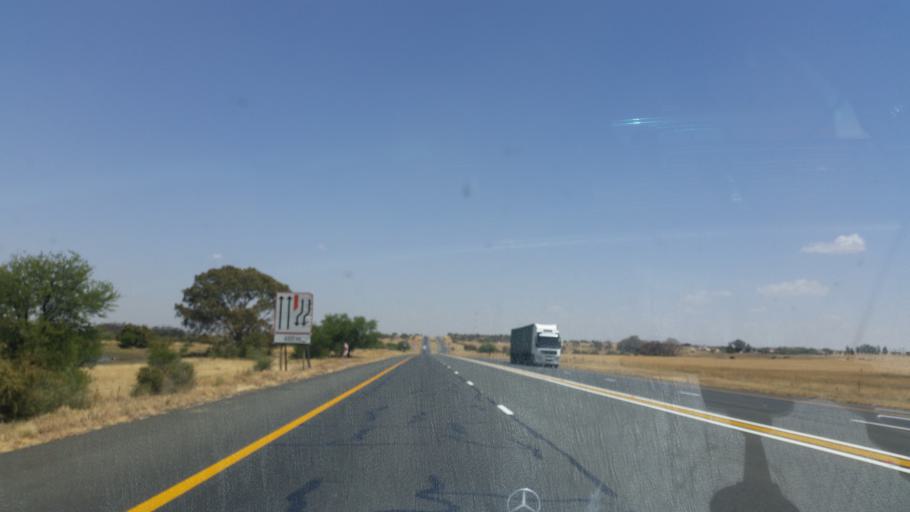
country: ZA
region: Orange Free State
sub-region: Lejweleputswa District Municipality
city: Brandfort
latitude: -28.8992
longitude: 26.4718
